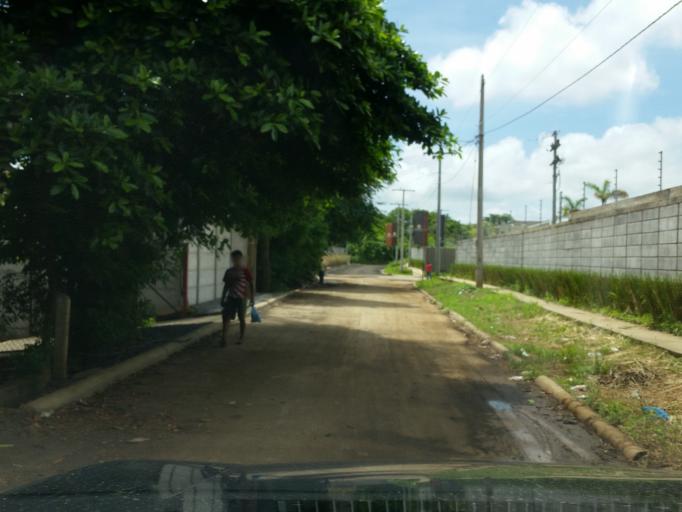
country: NI
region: Masaya
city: Ticuantepe
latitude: 12.0697
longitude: -86.2383
